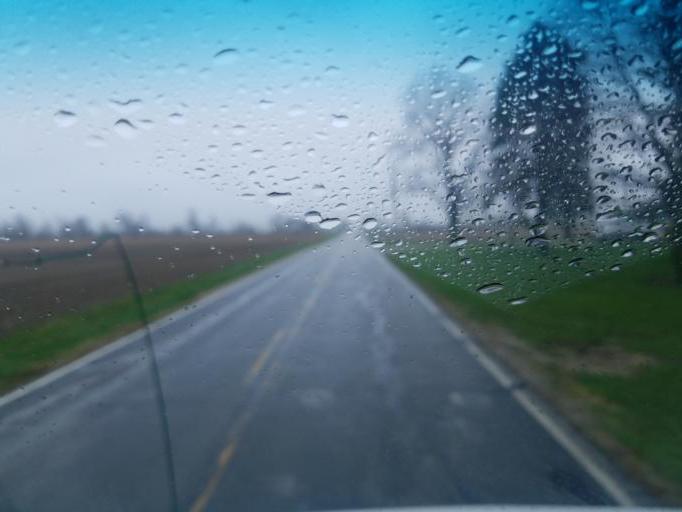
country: US
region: Ohio
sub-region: Wood County
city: North Baltimore
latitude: 41.1756
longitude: -83.6311
